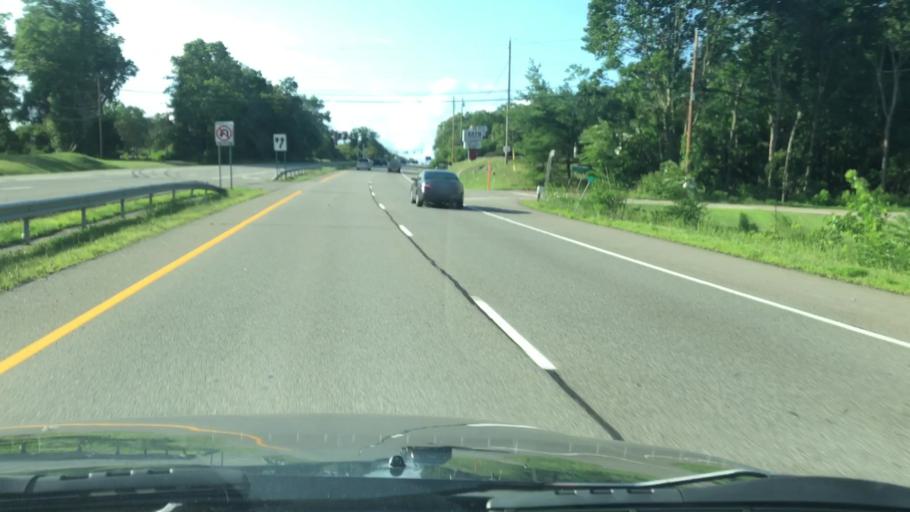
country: US
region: New York
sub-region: Dutchess County
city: Fishkill
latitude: 41.5433
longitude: -73.9026
